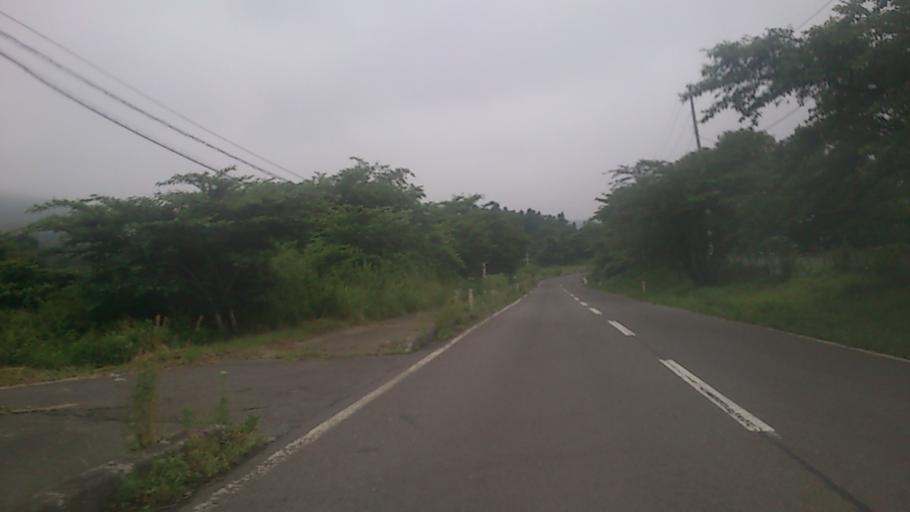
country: JP
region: Miyagi
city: Shiroishi
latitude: 38.1065
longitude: 140.5647
